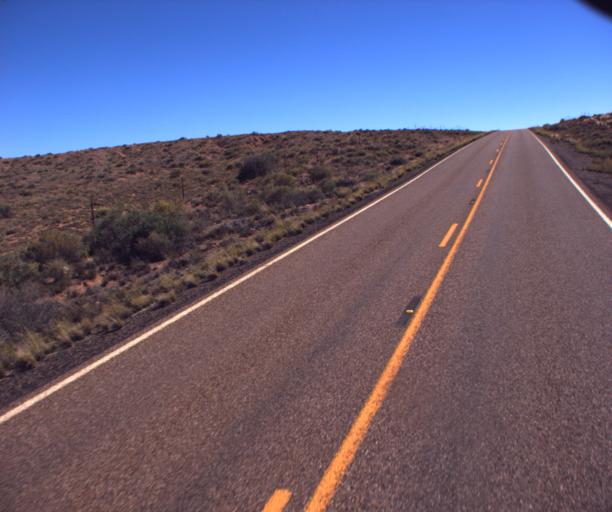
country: US
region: Arizona
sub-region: Navajo County
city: Holbrook
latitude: 35.0486
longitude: -110.0945
